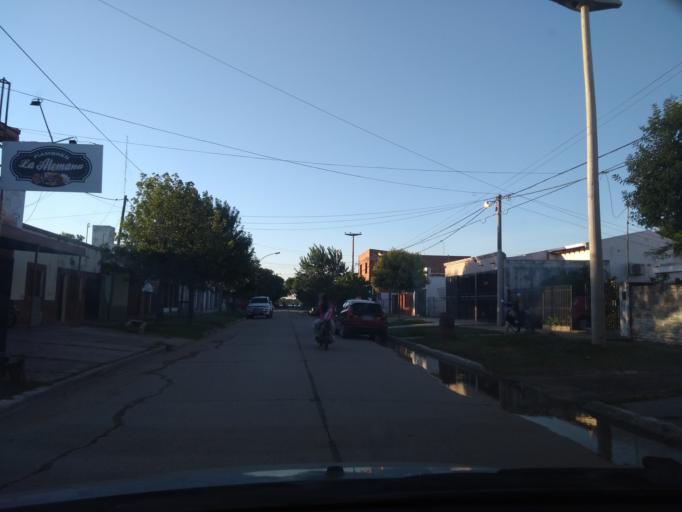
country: AR
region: Chaco
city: Barranqueras
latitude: -27.4820
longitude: -58.9373
